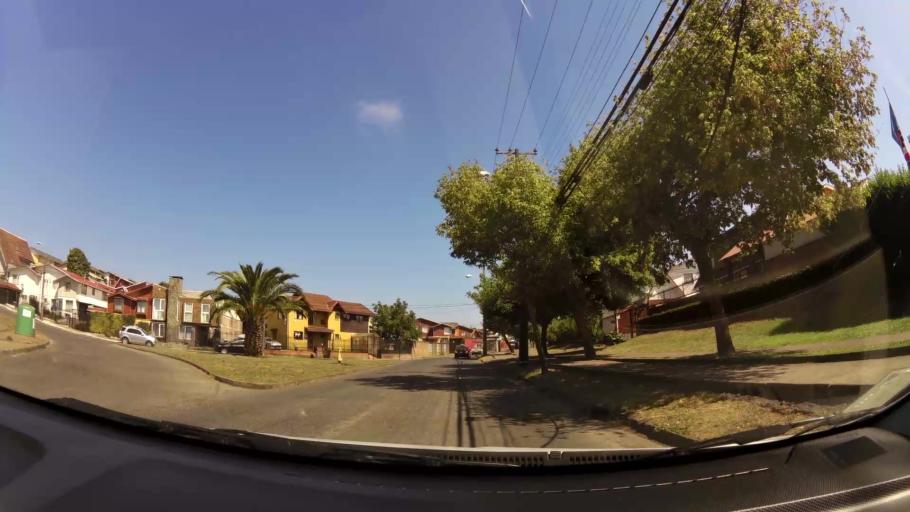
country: CL
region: Biobio
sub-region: Provincia de Concepcion
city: Concepcion
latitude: -36.7823
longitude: -73.0422
